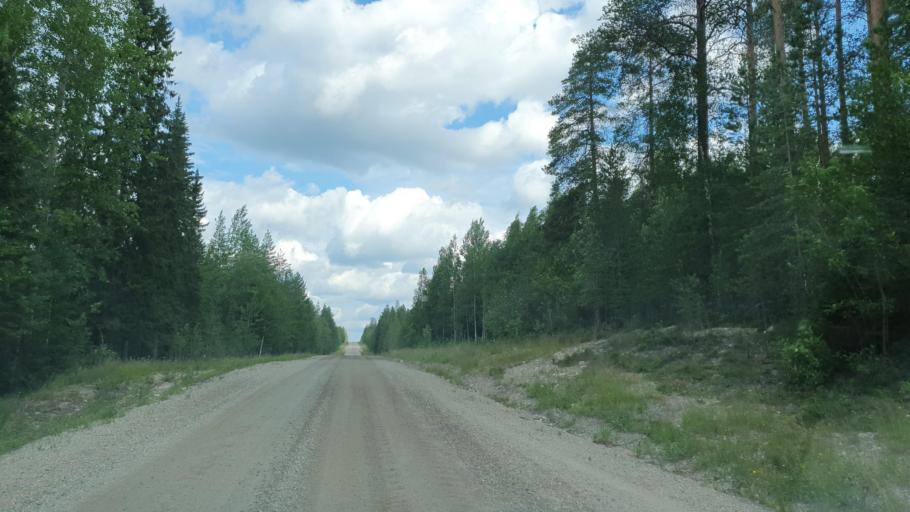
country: FI
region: Kainuu
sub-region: Kehys-Kainuu
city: Kuhmo
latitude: 64.4709
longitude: 29.5964
